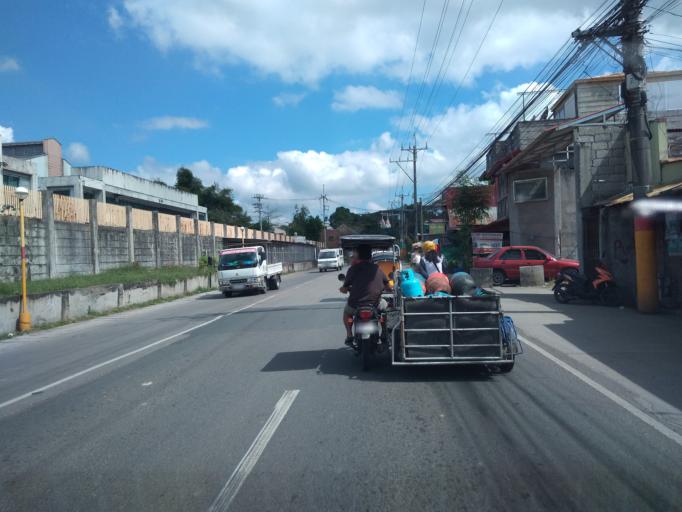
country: PH
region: Central Luzon
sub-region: Province of Bulacan
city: Guyong
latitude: 14.8333
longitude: 120.9748
